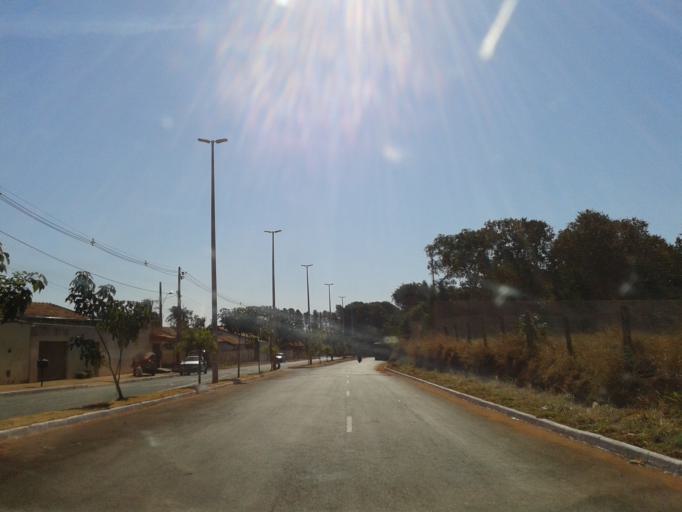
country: BR
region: Minas Gerais
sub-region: Ituiutaba
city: Ituiutaba
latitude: -18.9738
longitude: -49.4420
